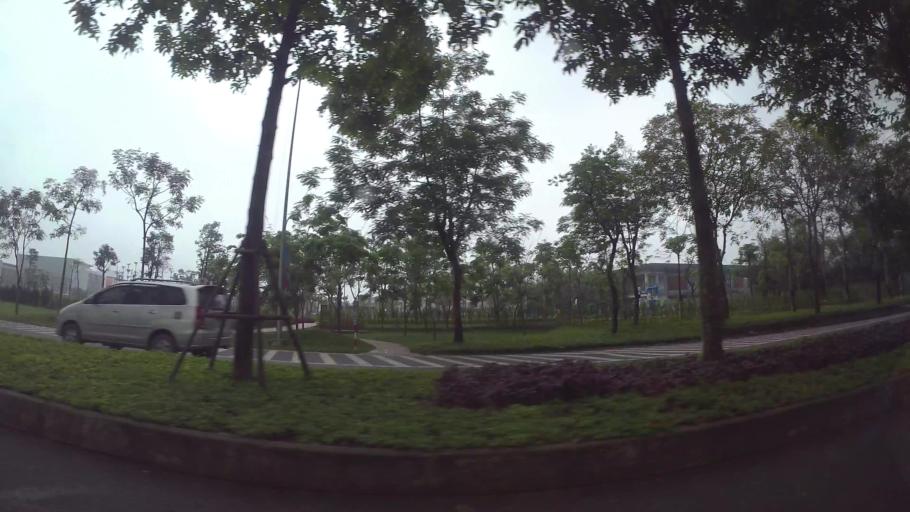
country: VN
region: Ha Noi
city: Van Dien
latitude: 20.9715
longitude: 105.8780
